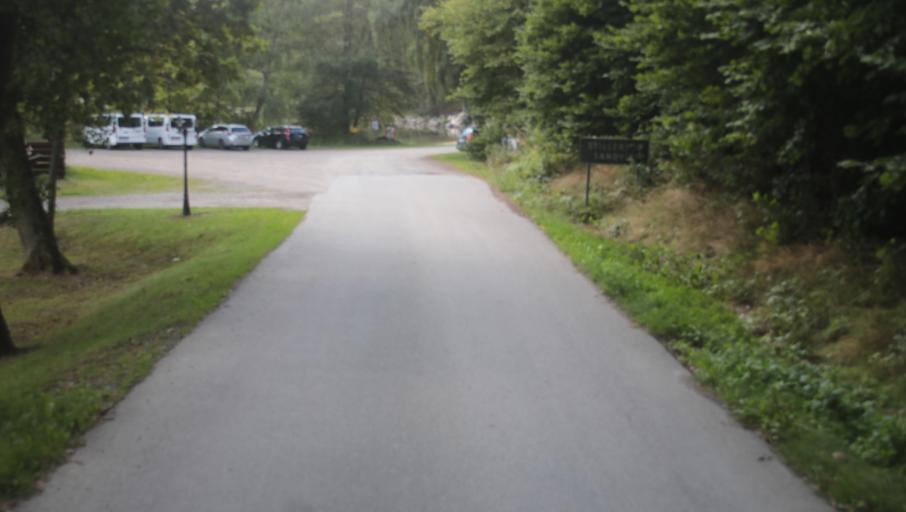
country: SE
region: Blekinge
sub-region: Karlshamns Kommun
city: Karlshamn
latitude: 56.1625
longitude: 14.8144
